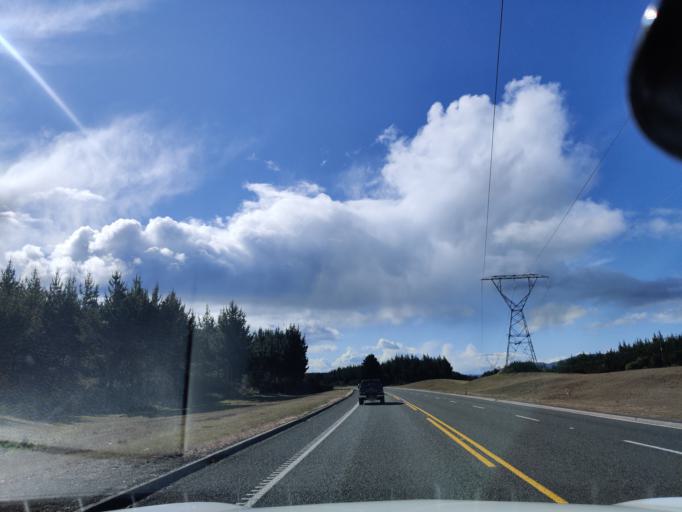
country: NZ
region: Waikato
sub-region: Taupo District
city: Taupo
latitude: -38.8102
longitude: 176.0789
